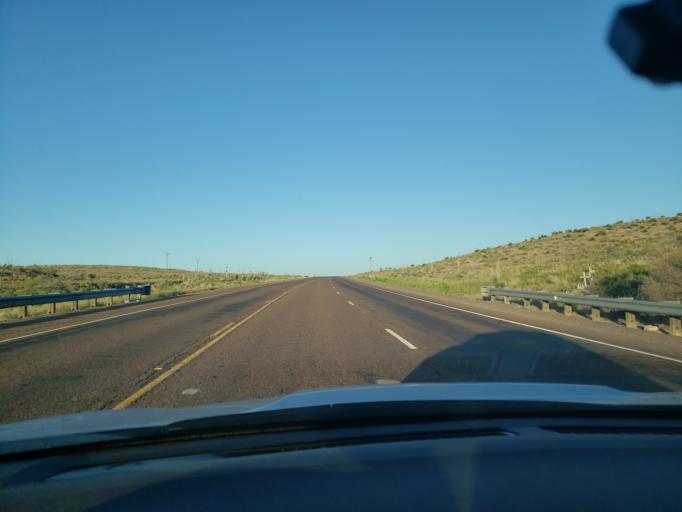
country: US
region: Texas
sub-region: El Paso County
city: Homestead Meadows South
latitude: 31.8273
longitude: -105.8899
